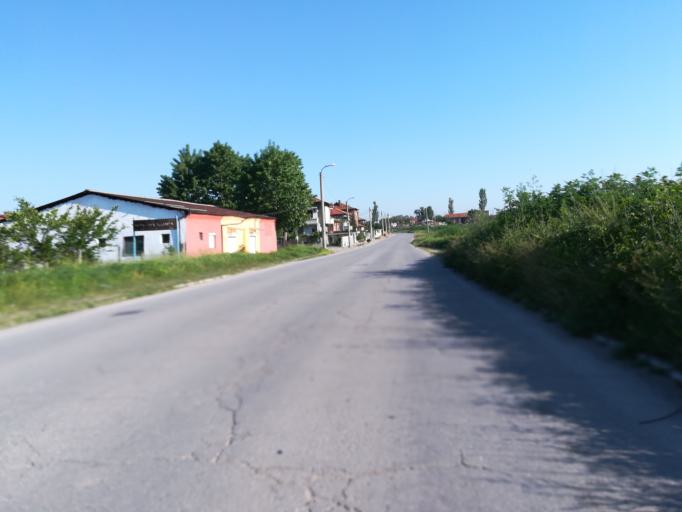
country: BG
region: Stara Zagora
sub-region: Obshtina Chirpan
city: Chirpan
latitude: 42.1054
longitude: 25.2275
